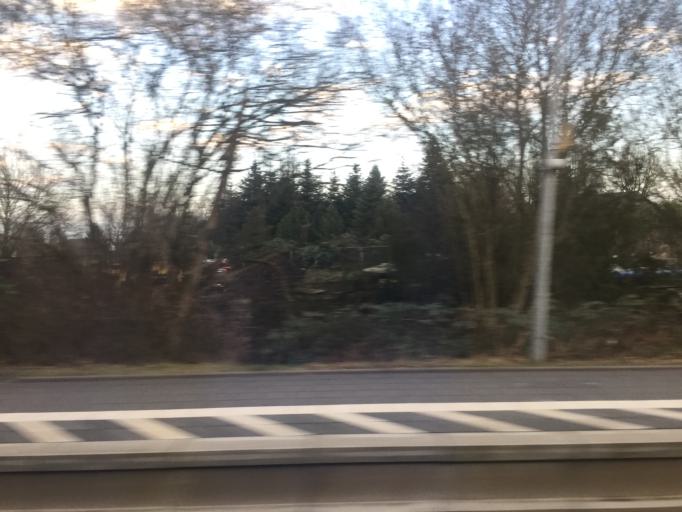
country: DE
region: Schleswig-Holstein
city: Prisdorf
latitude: 53.6759
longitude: 9.7591
